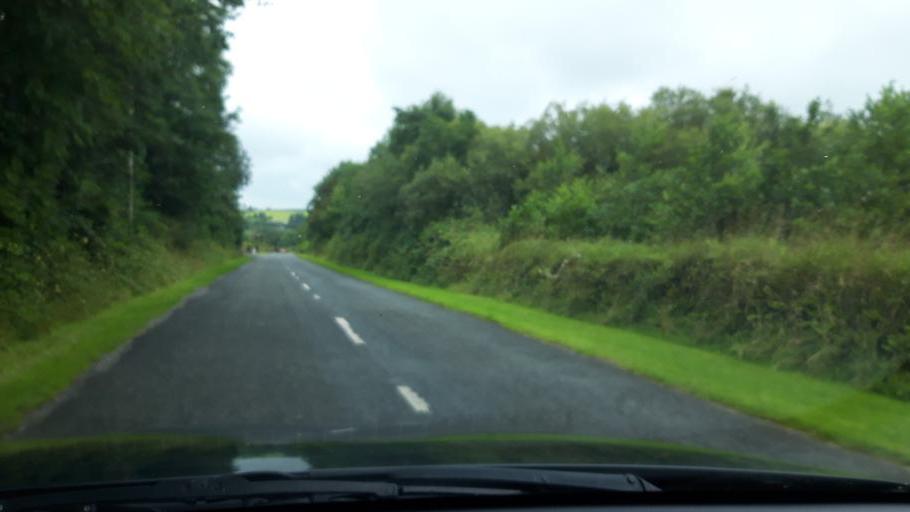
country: IE
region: Munster
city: Cahir
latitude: 52.1795
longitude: -7.8493
